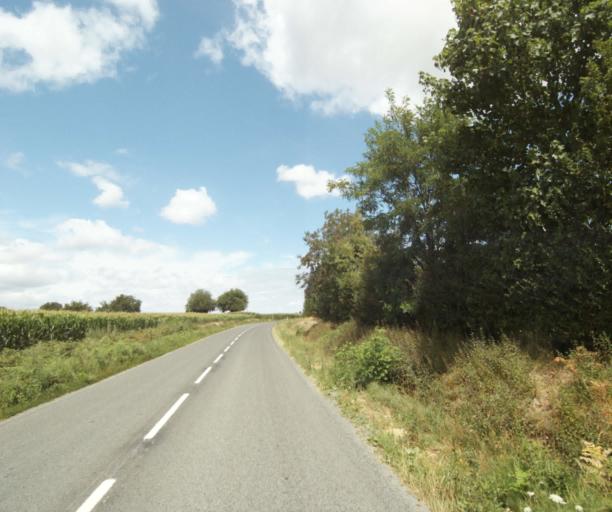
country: FR
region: Pays de la Loire
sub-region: Departement de la Sarthe
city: Sable-sur-Sarthe
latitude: 47.8624
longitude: -0.3341
